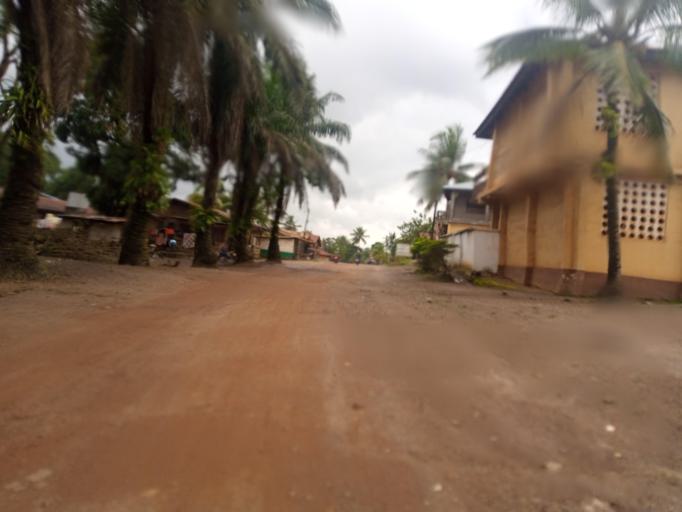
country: SL
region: Eastern Province
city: Kenema
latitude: 7.8611
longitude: -11.1924
